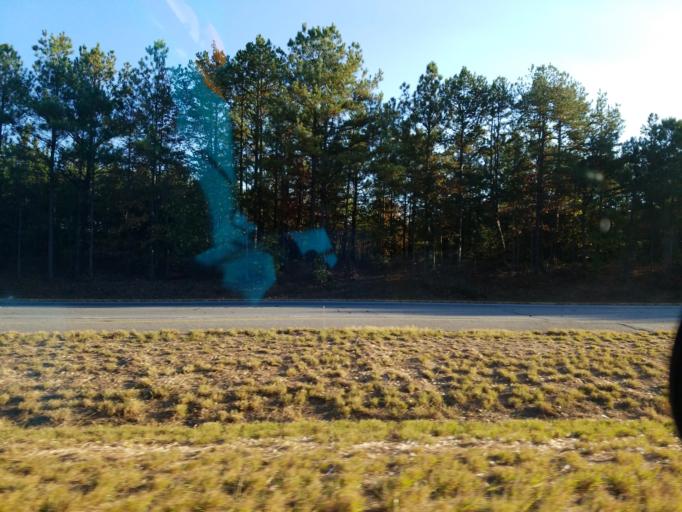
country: US
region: Georgia
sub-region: Bartow County
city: Euharlee
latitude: 34.2216
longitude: -84.9110
